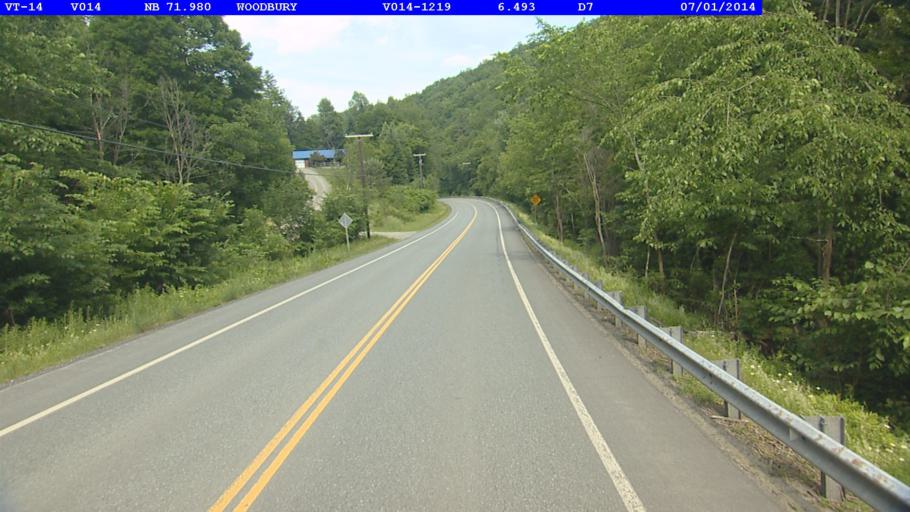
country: US
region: Vermont
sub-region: Caledonia County
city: Hardwick
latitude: 44.4742
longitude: -72.3983
